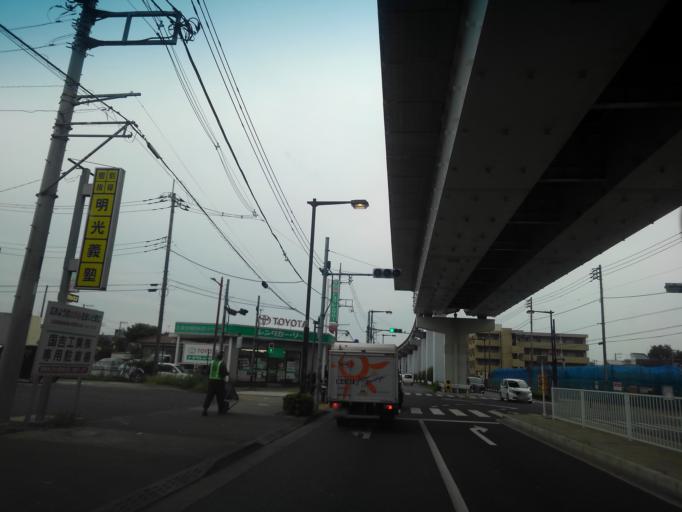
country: JP
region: Tokyo
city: Higashimurayama-shi
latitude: 35.7450
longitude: 139.4159
